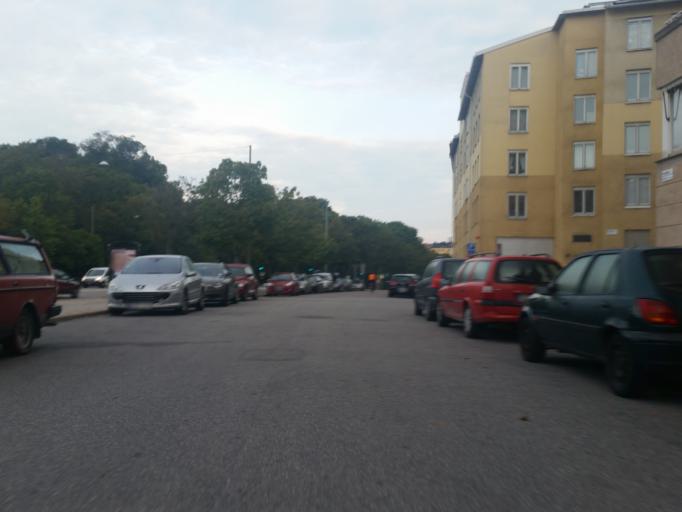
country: SE
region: Stockholm
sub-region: Stockholms Kommun
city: Arsta
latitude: 59.3122
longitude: 18.0549
